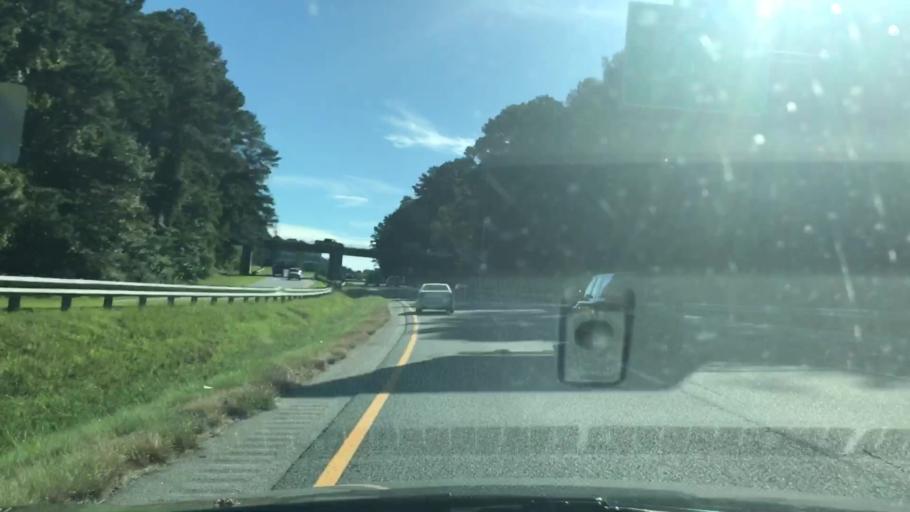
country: US
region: Georgia
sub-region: Gwinnett County
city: Mountain Park
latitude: 33.8224
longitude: -84.1338
